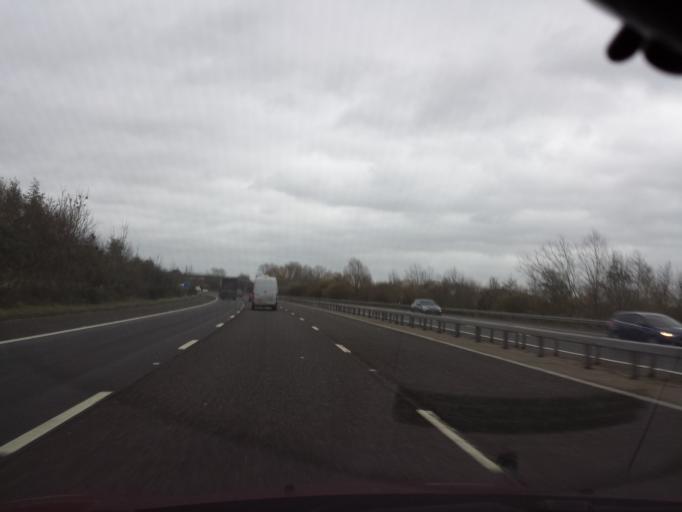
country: GB
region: England
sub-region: Surrey
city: Shepperton
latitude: 51.3948
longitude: -0.4608
